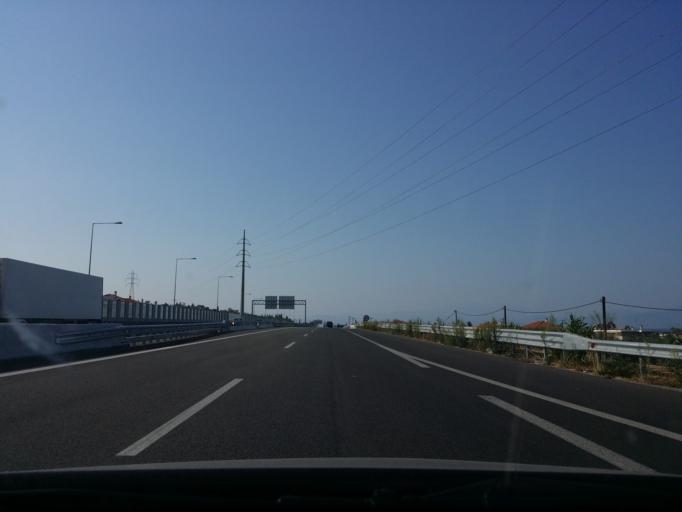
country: GR
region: Peloponnese
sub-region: Nomos Korinthias
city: Pasion
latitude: 38.0119
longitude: 22.7331
